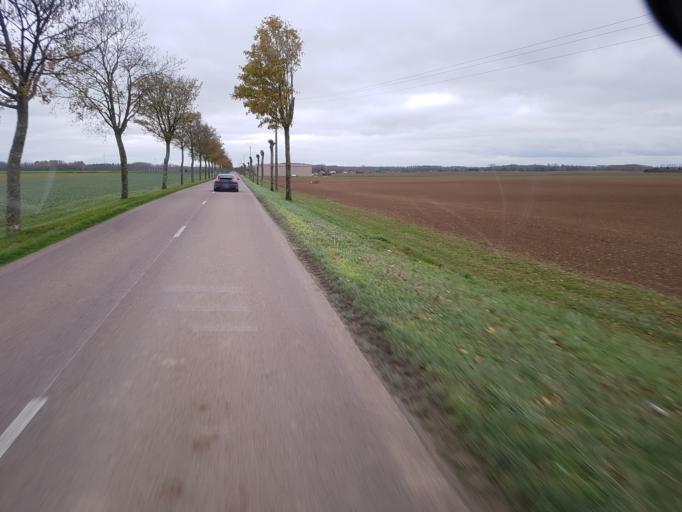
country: FR
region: Champagne-Ardenne
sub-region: Departement de l'Aube
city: Mery-sur-Seine
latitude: 48.5458
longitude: 3.8692
